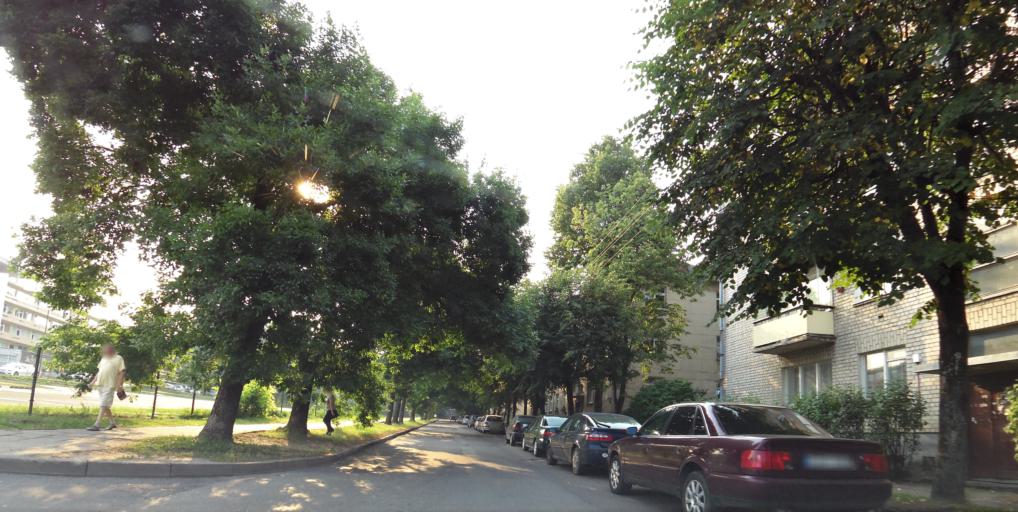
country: LT
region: Vilnius County
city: Rasos
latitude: 54.7083
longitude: 25.3156
